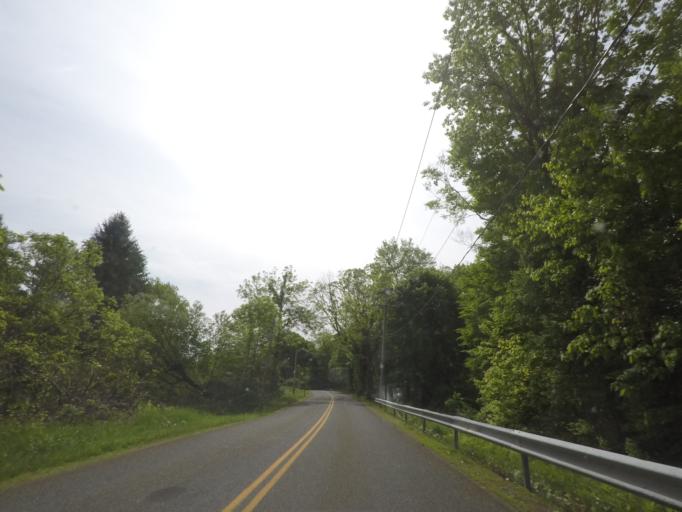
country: US
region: New York
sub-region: Saratoga County
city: Mechanicville
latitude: 42.9243
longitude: -73.7339
